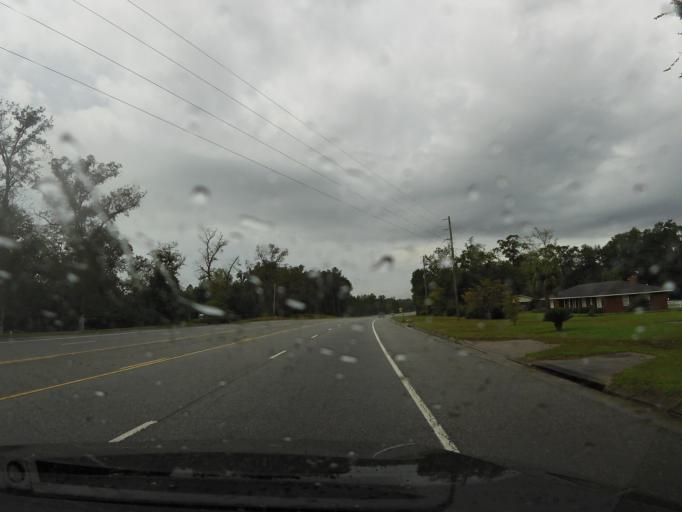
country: US
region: Georgia
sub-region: Wayne County
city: Jesup
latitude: 31.5615
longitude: -81.8340
